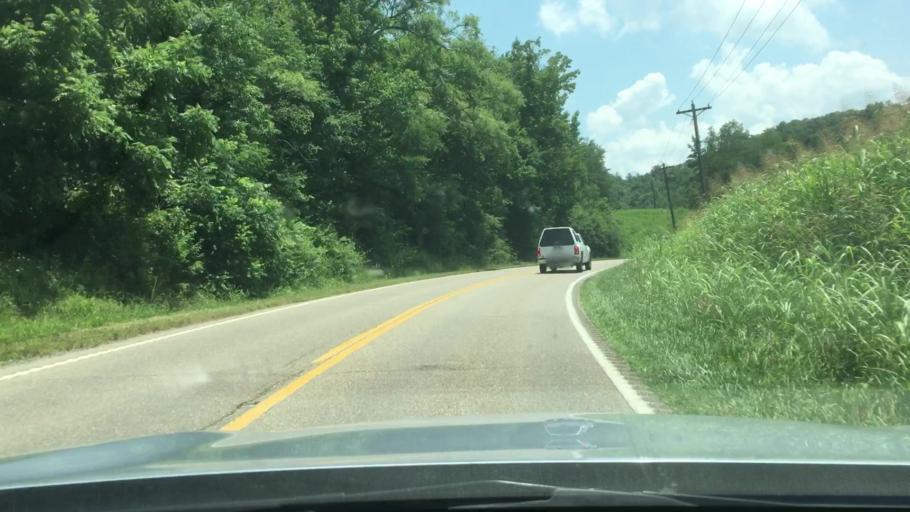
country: US
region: Tennessee
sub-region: Cocke County
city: Newport
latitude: 35.9335
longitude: -83.0383
